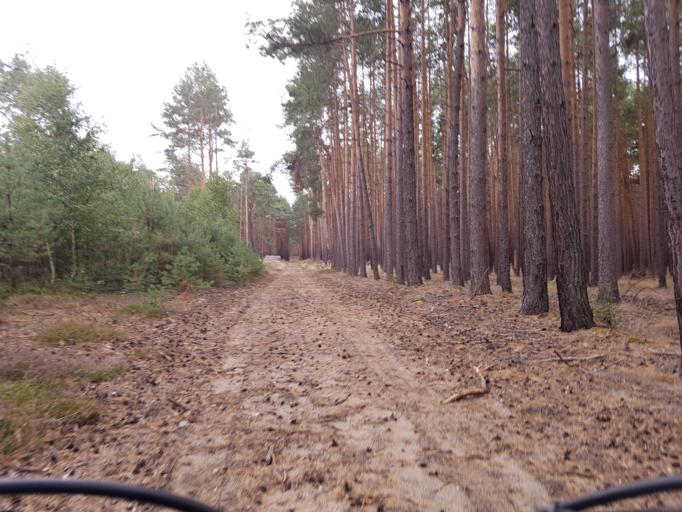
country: DE
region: Brandenburg
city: Trobitz
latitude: 51.5641
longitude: 13.4375
